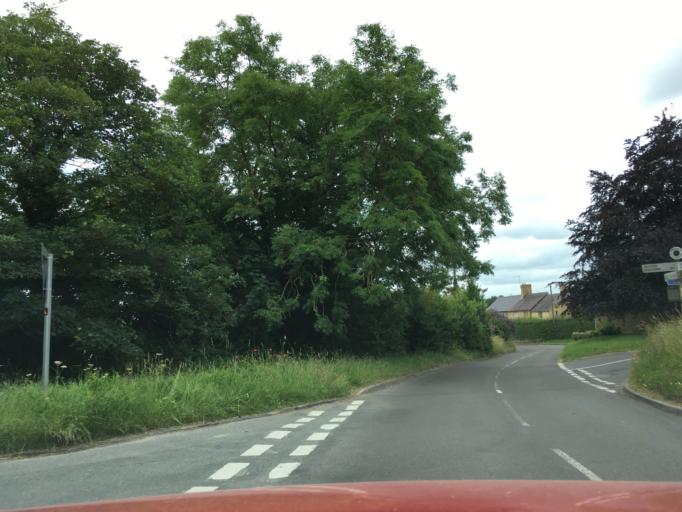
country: GB
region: England
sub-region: Oxfordshire
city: Charlbury
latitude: 51.8938
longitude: -1.4922
